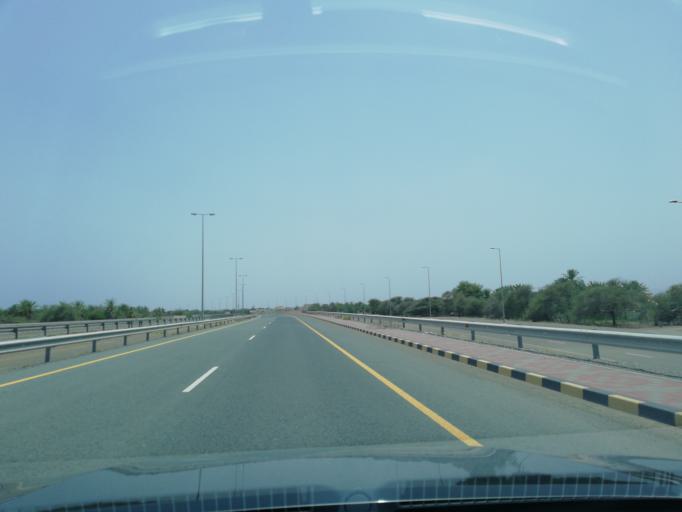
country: OM
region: Al Batinah
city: Shinas
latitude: 24.7972
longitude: 56.4515
